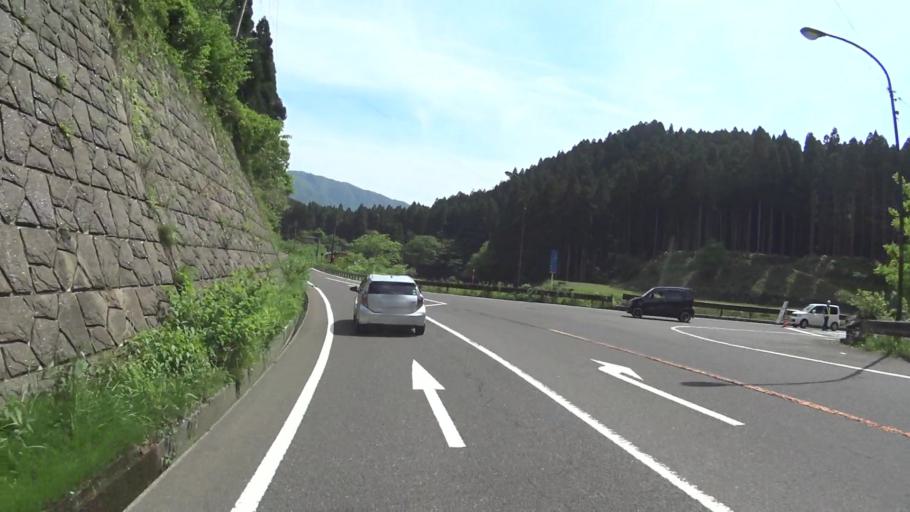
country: JP
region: Shiga Prefecture
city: Kitahama
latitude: 35.3673
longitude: 135.9191
